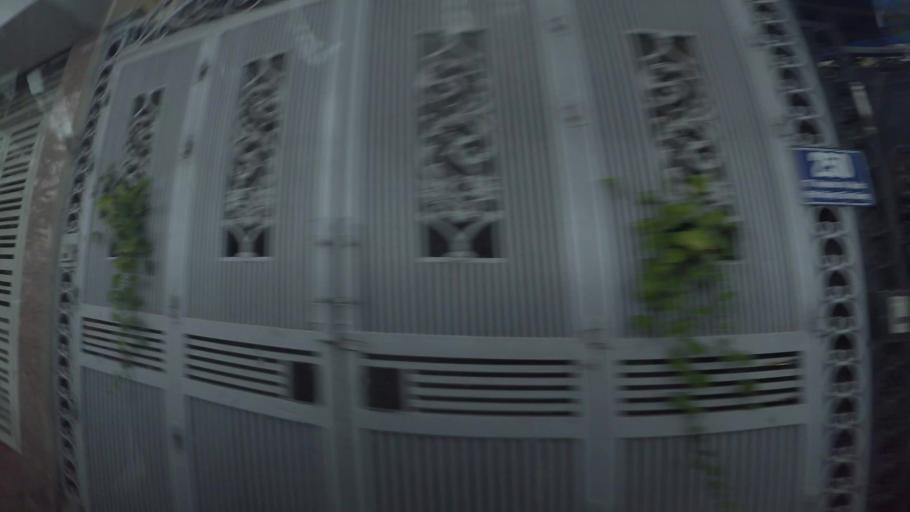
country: VN
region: Ha Noi
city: Dong Da
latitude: 21.0167
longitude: 105.8190
